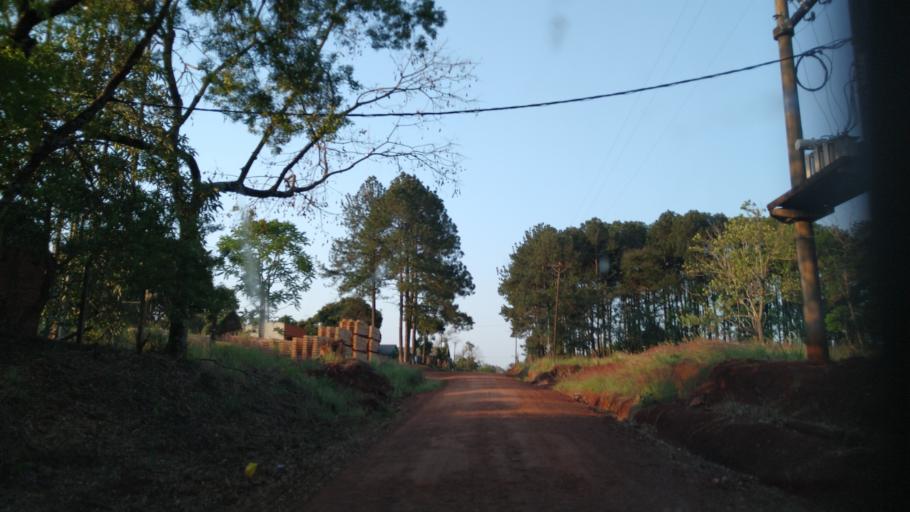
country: AR
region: Misiones
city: Jardin America
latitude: -27.0714
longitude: -55.2686
